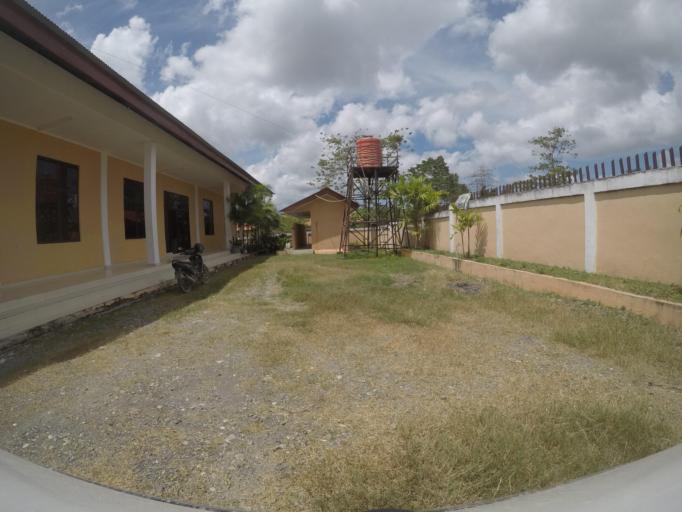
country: TL
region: Viqueque
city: Viqueque
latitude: -8.8516
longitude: 126.3612
